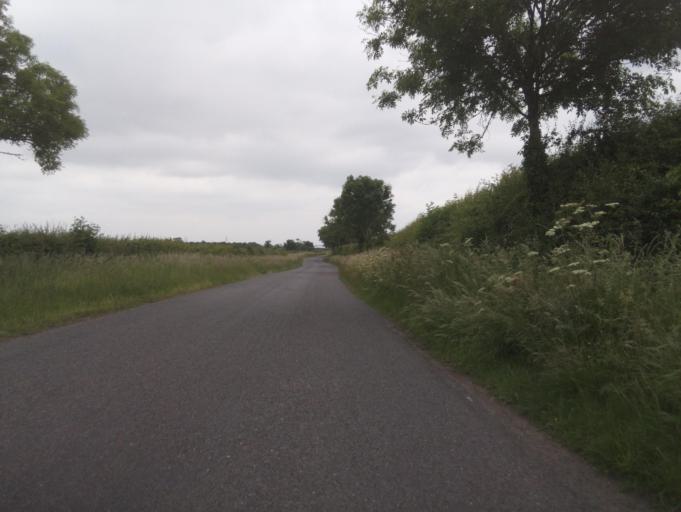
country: GB
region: England
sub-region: District of Rutland
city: Langham
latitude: 52.6707
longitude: -0.7657
